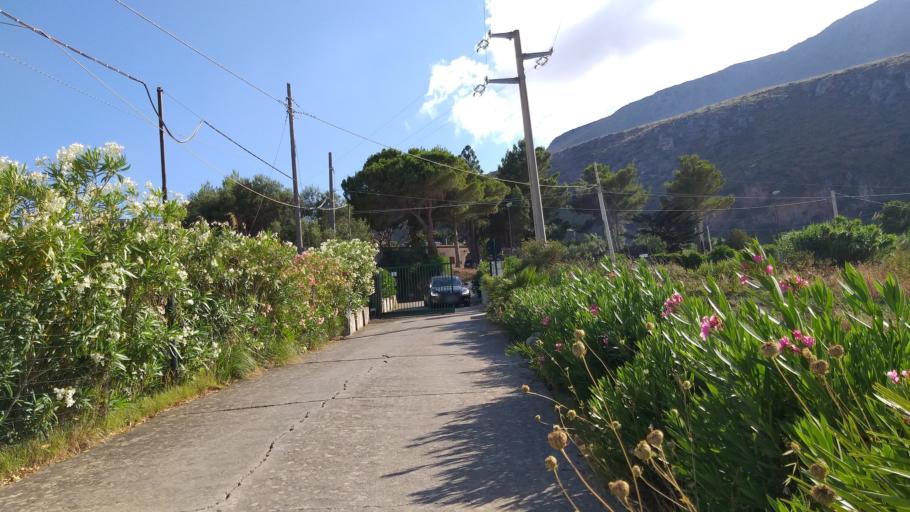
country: IT
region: Sicily
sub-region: Trapani
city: Castelluzzo
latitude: 38.0752
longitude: 12.8090
